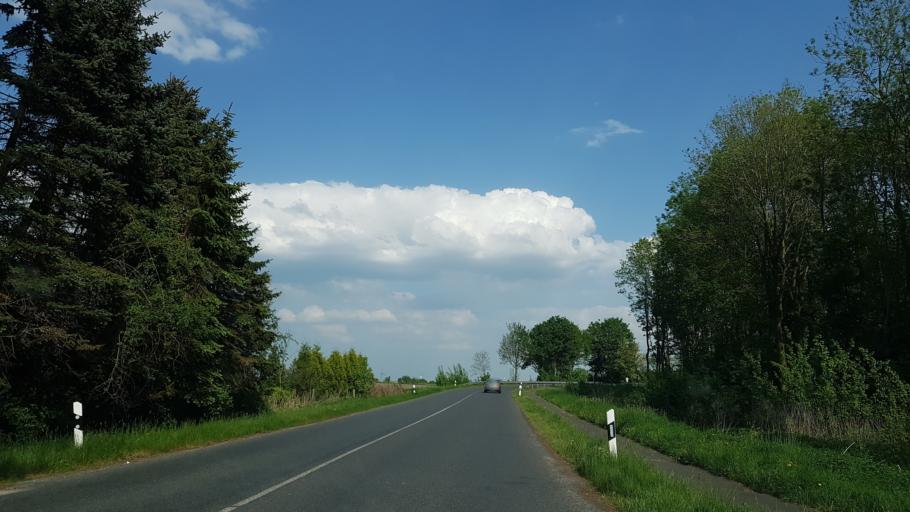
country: DE
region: Lower Saxony
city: Langen
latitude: 53.6447
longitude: 8.6092
